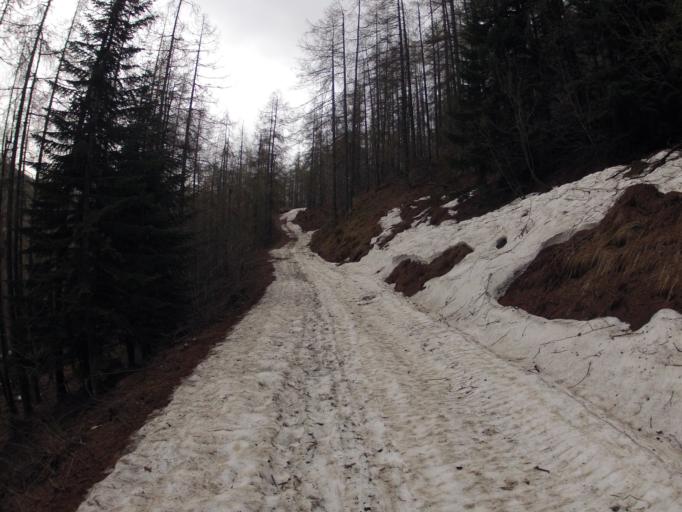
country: IT
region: Piedmont
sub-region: Provincia di Cuneo
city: Crissolo
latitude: 44.7000
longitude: 7.1390
